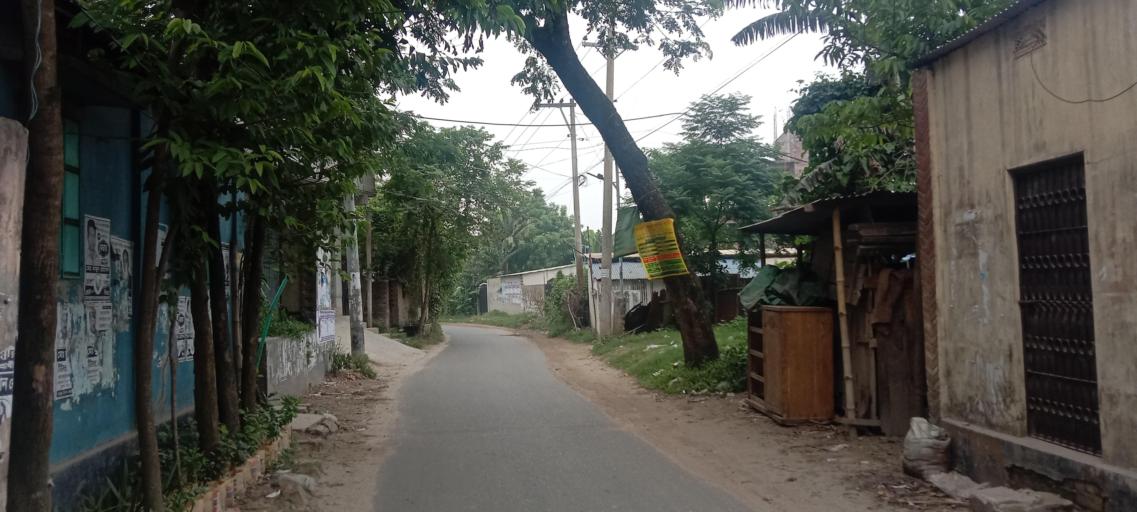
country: BD
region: Dhaka
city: Azimpur
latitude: 23.7346
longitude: 90.3227
